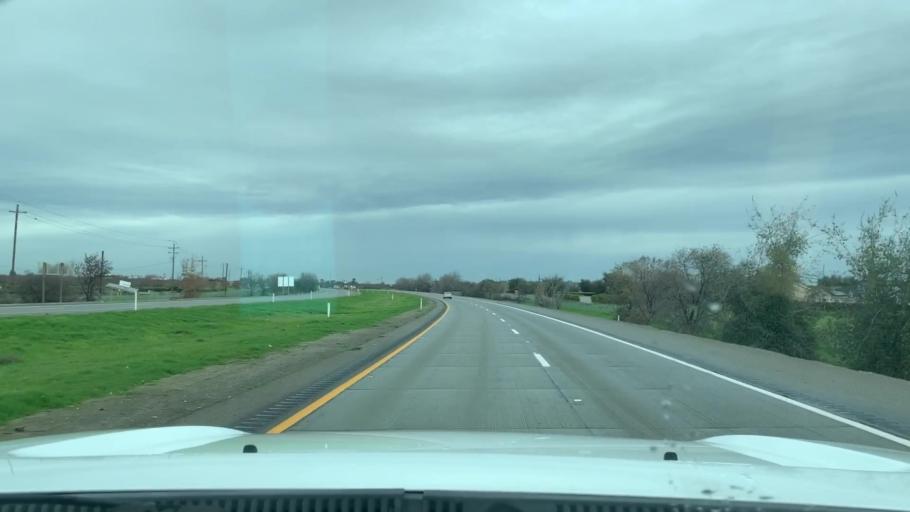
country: US
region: California
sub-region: Kings County
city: Lemoore
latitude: 36.3058
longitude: -119.8087
